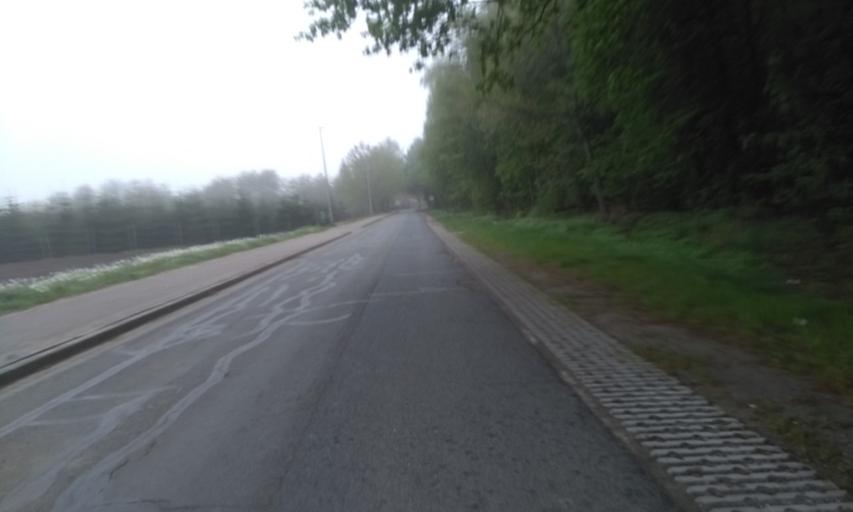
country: DE
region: Lower Saxony
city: Nottensdorf
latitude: 53.4733
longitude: 9.6163
